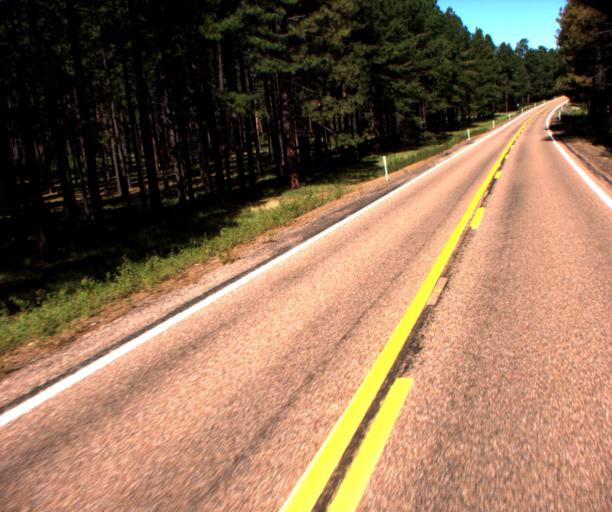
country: US
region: Arizona
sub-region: Navajo County
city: Pinetop-Lakeside
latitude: 34.0634
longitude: -109.7729
